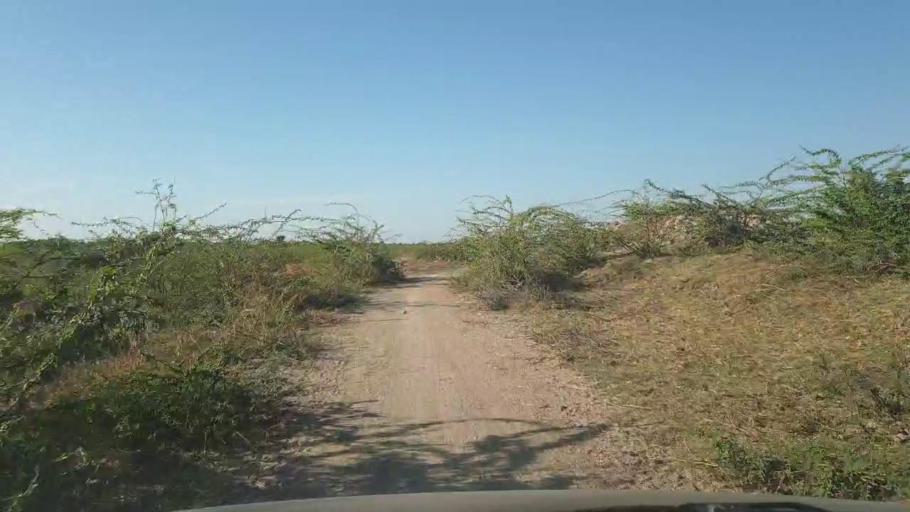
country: PK
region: Sindh
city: Dhoro Naro
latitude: 25.4339
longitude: 69.5517
